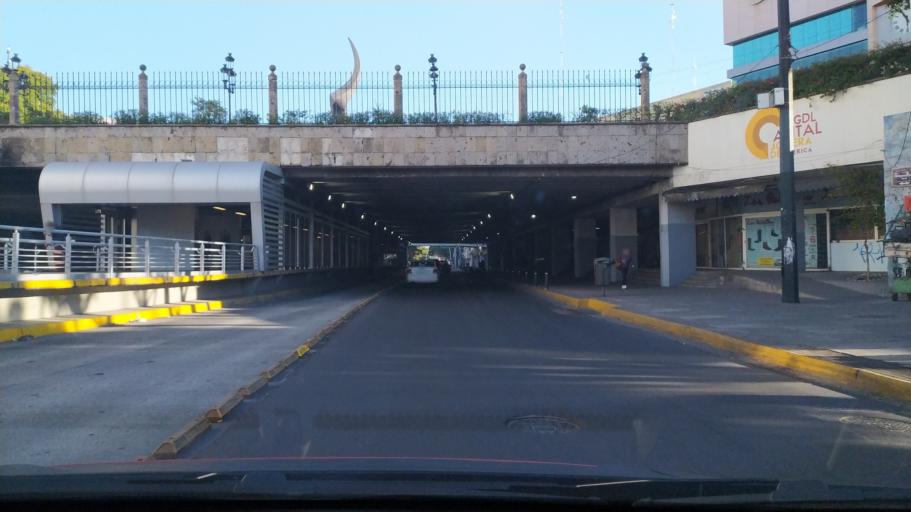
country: MX
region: Jalisco
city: Guadalajara
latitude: 20.6763
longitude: -103.3412
